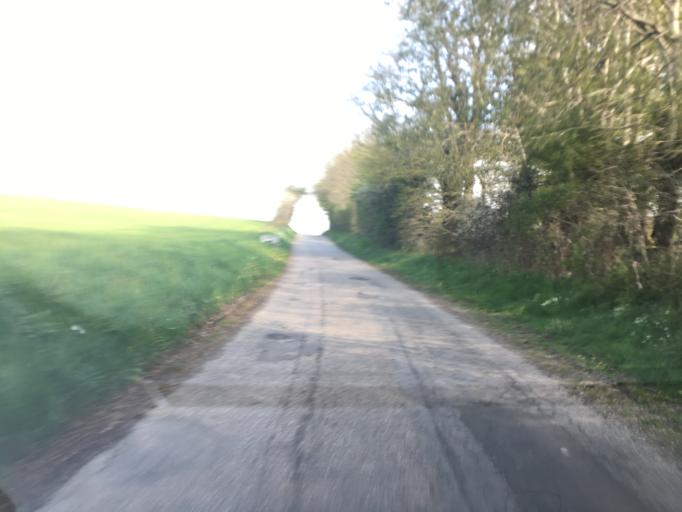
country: DK
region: South Denmark
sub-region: Haderslev Kommune
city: Vojens
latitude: 55.1930
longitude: 9.3899
